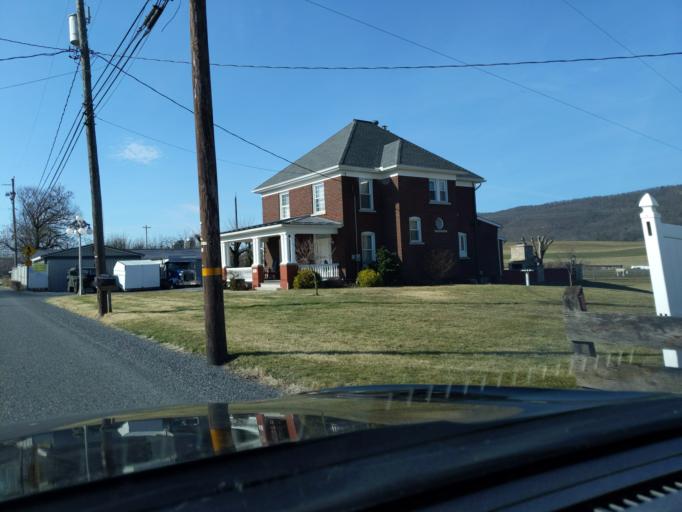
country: US
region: Pennsylvania
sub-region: Blair County
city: Williamsburg
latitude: 40.4046
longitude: -78.2754
